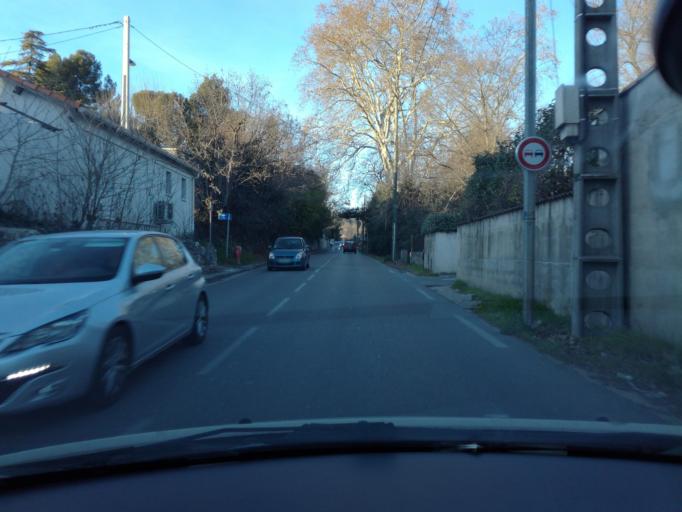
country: FR
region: Provence-Alpes-Cote d'Azur
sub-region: Departement des Bouches-du-Rhone
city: La Penne-sur-Huveaune
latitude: 43.3006
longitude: 5.5015
